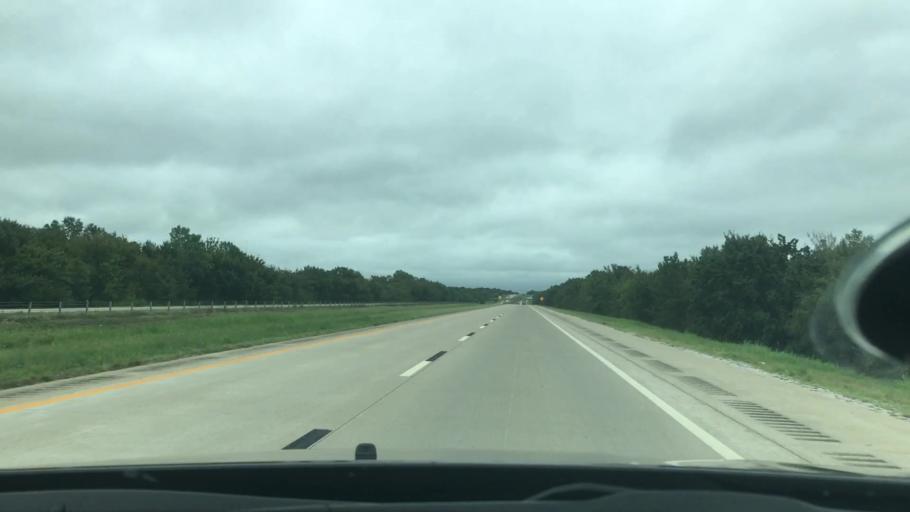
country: US
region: Oklahoma
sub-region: Muskogee County
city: Warner
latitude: 35.4823
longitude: -95.2553
